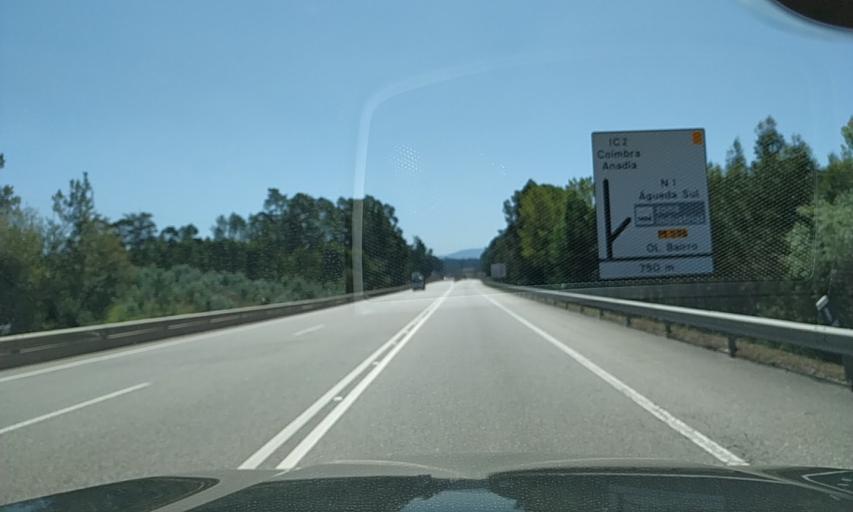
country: PT
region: Aveiro
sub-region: Agueda
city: Aguada de Cima
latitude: 40.5282
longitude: -8.4541
